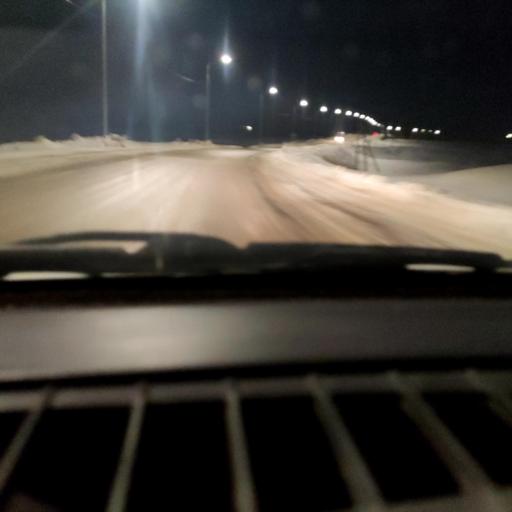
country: RU
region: Bashkortostan
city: Ulukulevo
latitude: 54.5685
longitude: 56.3334
